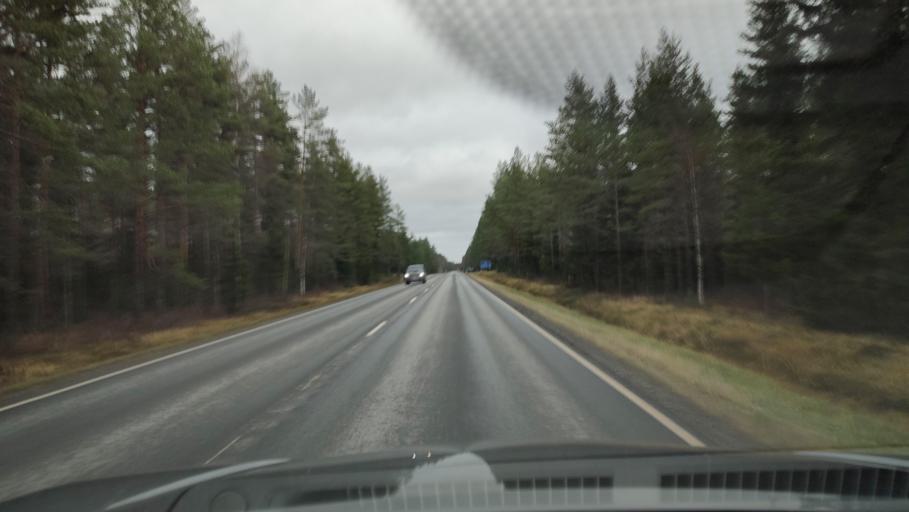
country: FI
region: Southern Ostrobothnia
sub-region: Seinaejoki
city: Kurikka
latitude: 62.5337
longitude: 22.3308
